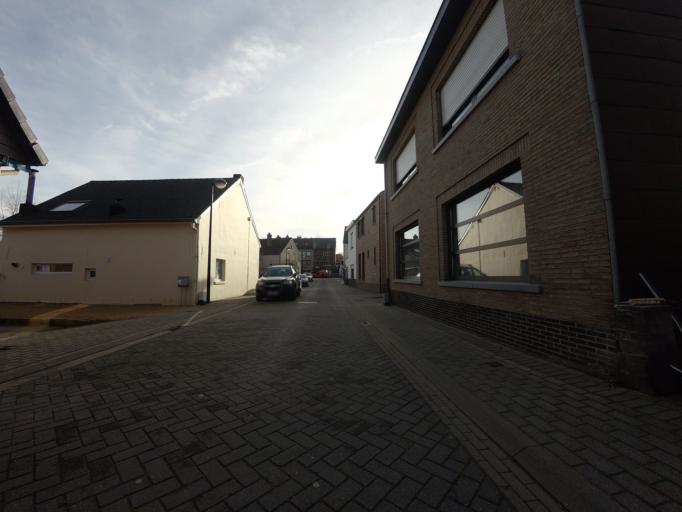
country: BE
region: Flanders
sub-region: Provincie Vlaams-Brabant
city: Kortenberg
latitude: 50.8779
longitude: 4.5498
